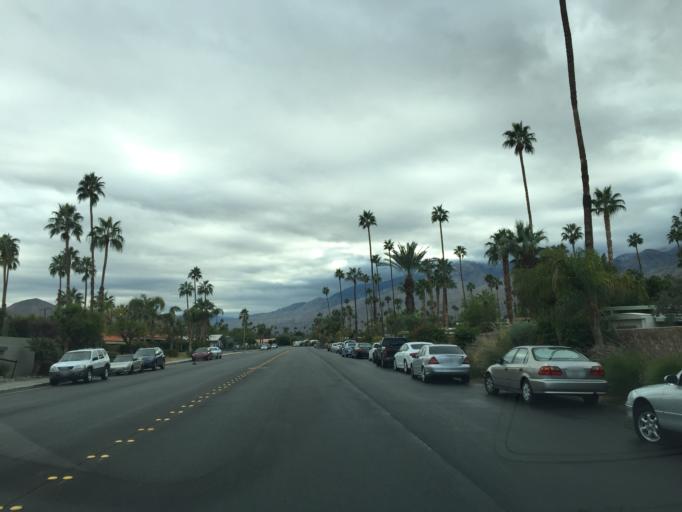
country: US
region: California
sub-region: Riverside County
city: Palm Springs
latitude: 33.7994
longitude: -116.5392
